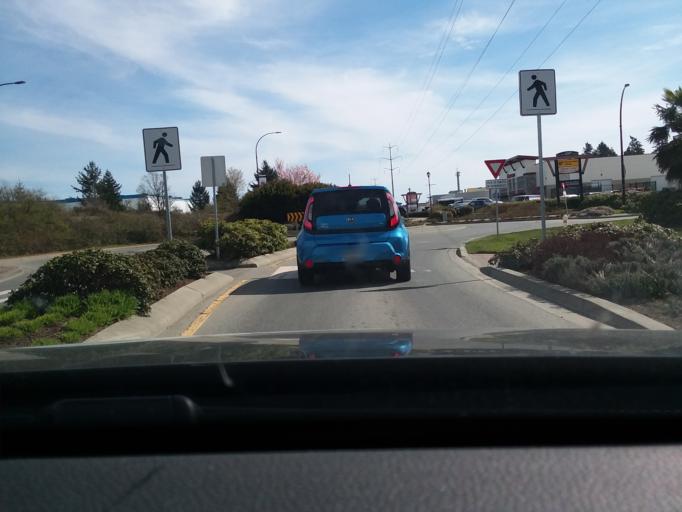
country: CA
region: British Columbia
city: Langford
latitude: 48.4435
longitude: -123.5206
